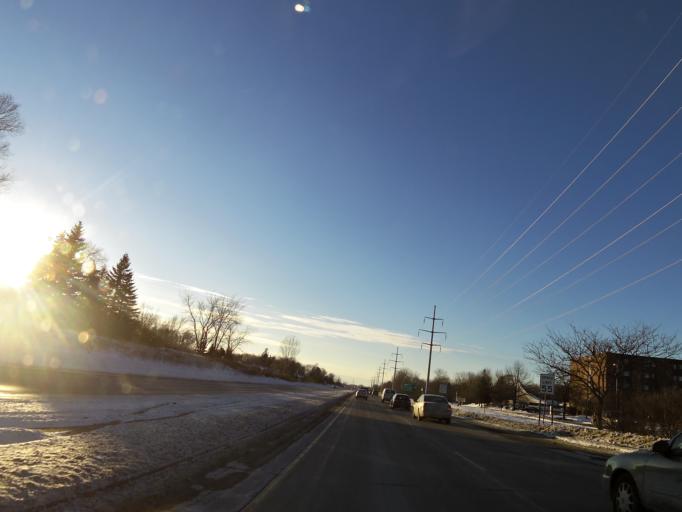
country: US
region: Minnesota
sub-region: Hennepin County
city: Eden Prairie
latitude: 44.8628
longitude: -93.4886
